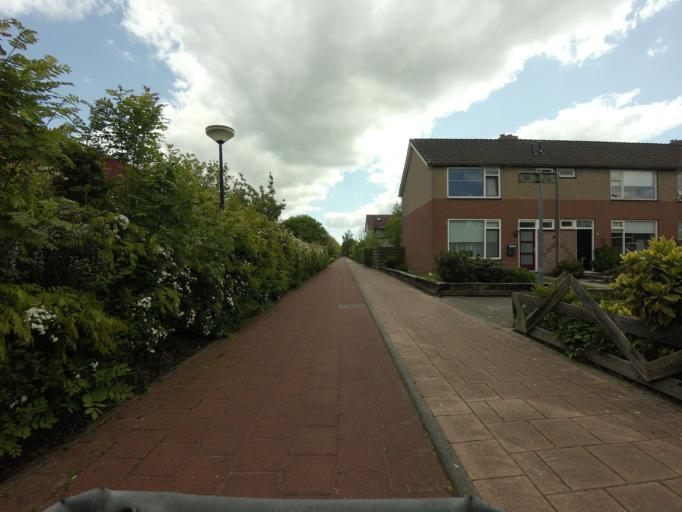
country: NL
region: Friesland
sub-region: Sudwest Fryslan
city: Bolsward
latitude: 53.0694
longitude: 5.5314
